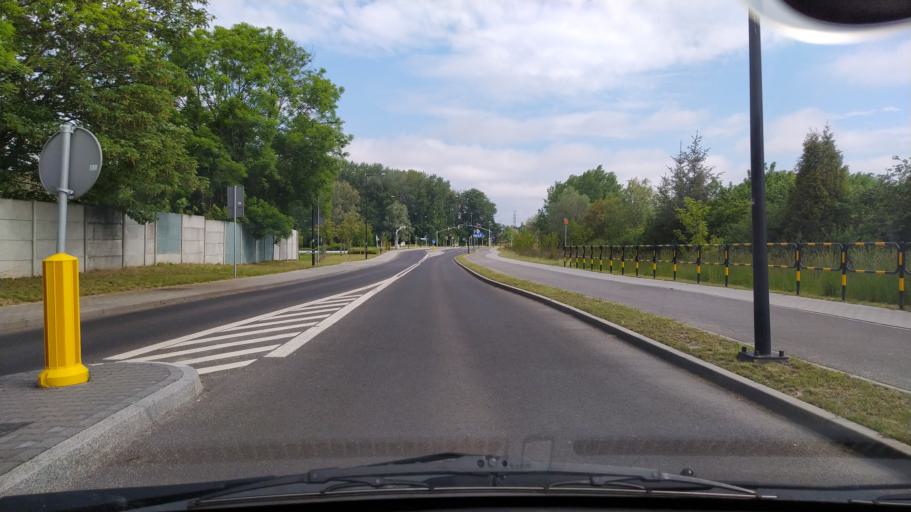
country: PL
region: Silesian Voivodeship
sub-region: Gliwice
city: Gliwice
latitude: 50.2841
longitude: 18.6918
